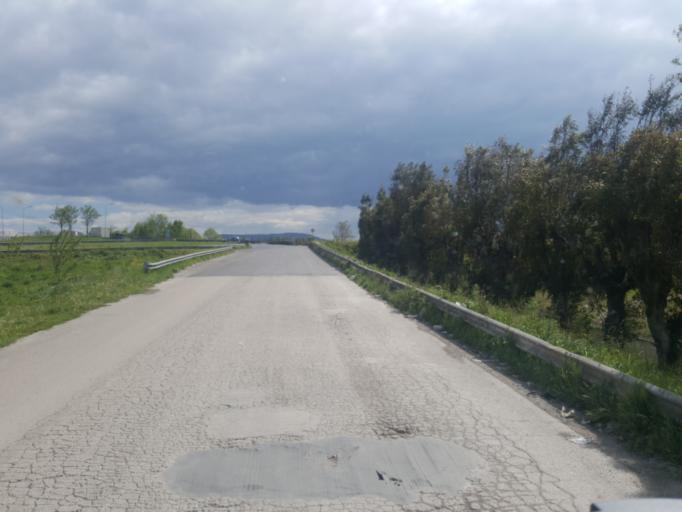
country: IT
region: Campania
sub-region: Provincia di Napoli
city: Torretta-Scalzapecora
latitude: 40.9330
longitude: 14.1220
